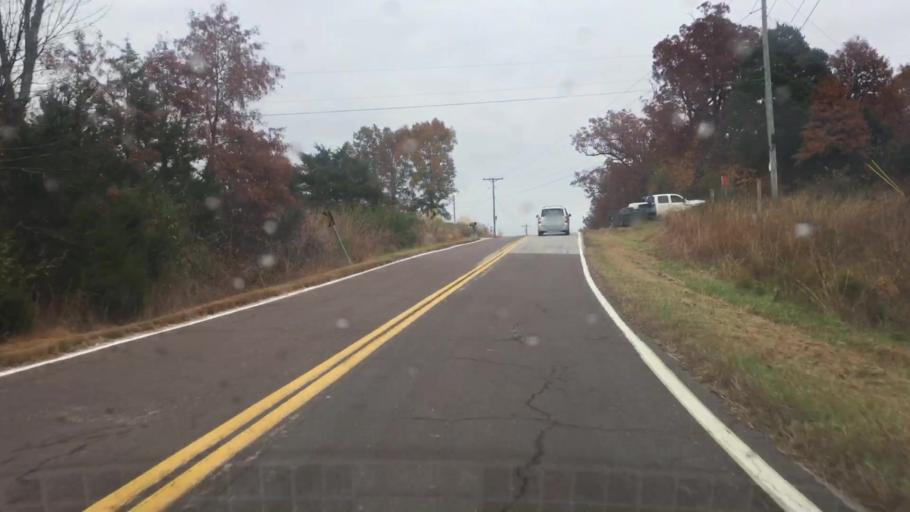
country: US
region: Missouri
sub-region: Callaway County
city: Fulton
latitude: 38.7879
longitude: -91.7886
